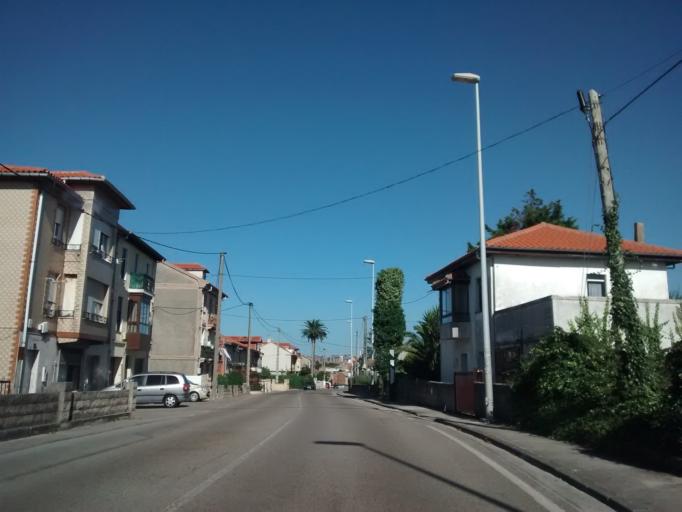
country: ES
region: Cantabria
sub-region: Provincia de Cantabria
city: Santander
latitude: 43.4653
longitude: -3.8475
